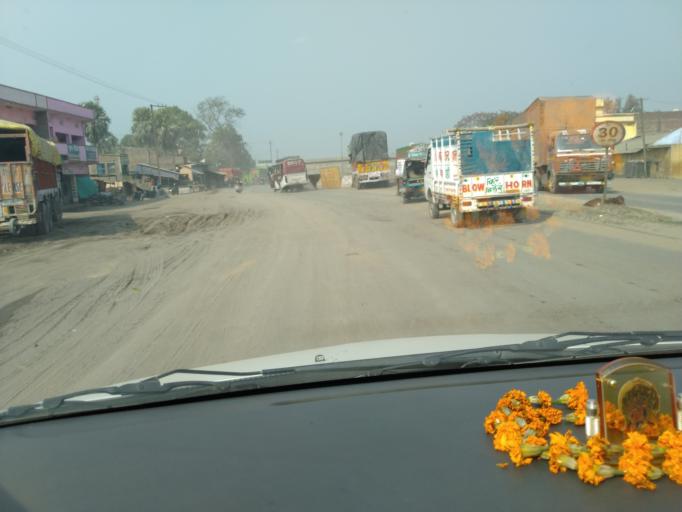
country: IN
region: Bihar
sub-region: Rohtas
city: Dehri
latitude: 24.9147
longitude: 84.1597
